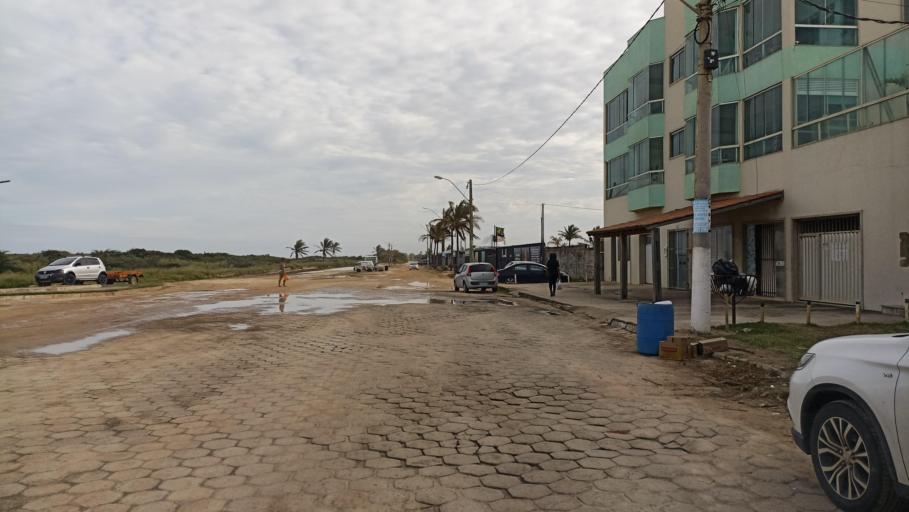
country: BR
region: Espirito Santo
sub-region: Sao Mateus
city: Sao Mateus
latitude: -18.7527
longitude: -39.7481
